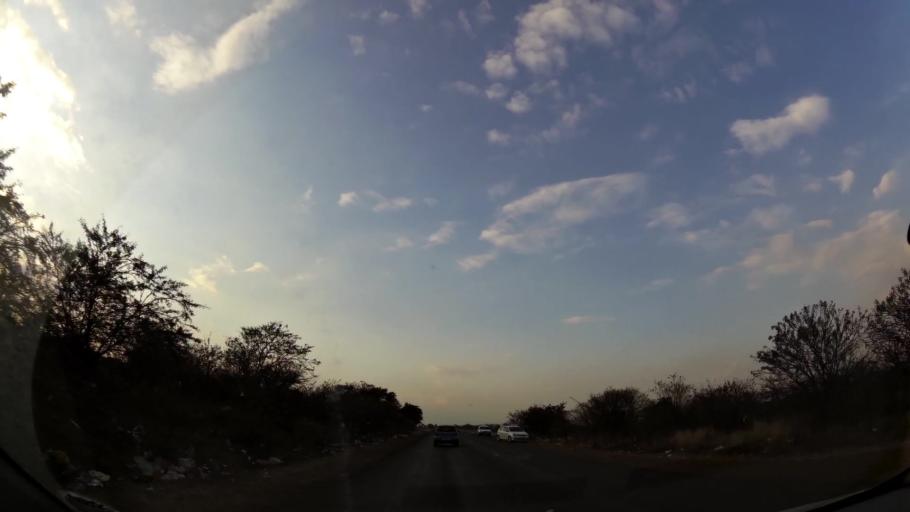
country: ZA
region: Gauteng
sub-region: City of Johannesburg Metropolitan Municipality
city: Orange Farm
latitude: -26.5848
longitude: 27.8545
